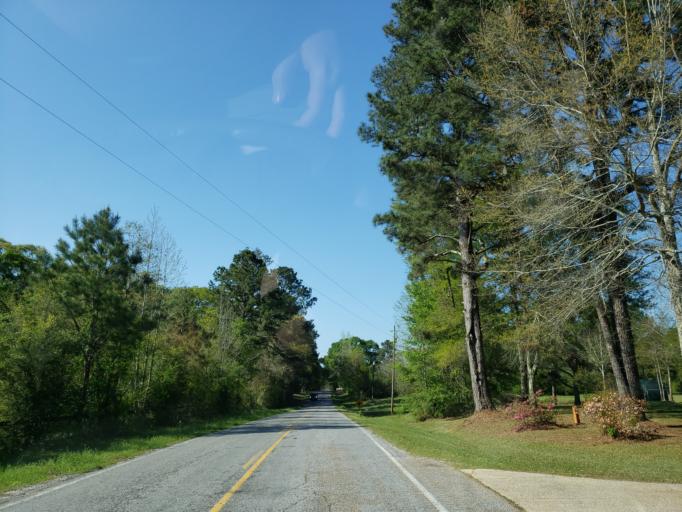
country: US
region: Mississippi
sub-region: Forrest County
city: Rawls Springs
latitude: 31.5266
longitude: -89.3592
